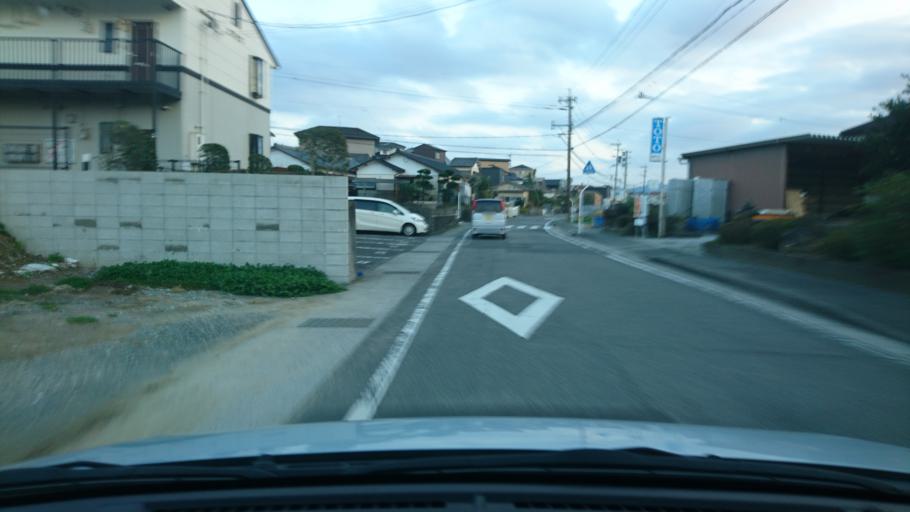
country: JP
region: Miyazaki
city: Miyazaki-shi
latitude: 31.8651
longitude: 131.4269
